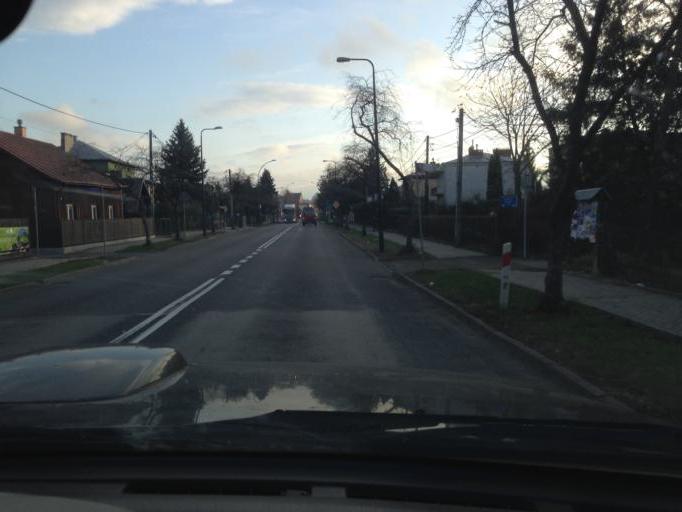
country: PL
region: Subcarpathian Voivodeship
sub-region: Powiat jasielski
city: Jaslo
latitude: 49.7548
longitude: 21.4731
